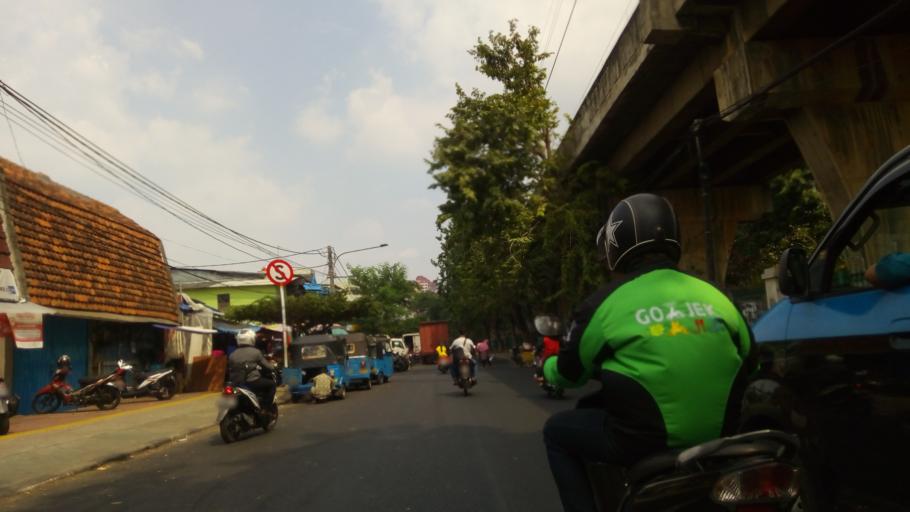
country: ID
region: Jakarta Raya
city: Jakarta
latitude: -6.1563
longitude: 106.8276
